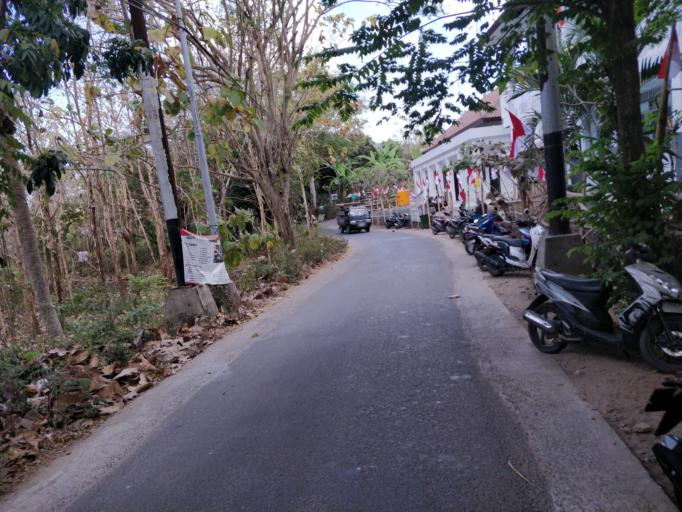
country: ID
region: Bali
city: Lembongan Kawan
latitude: -8.6864
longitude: 115.4426
